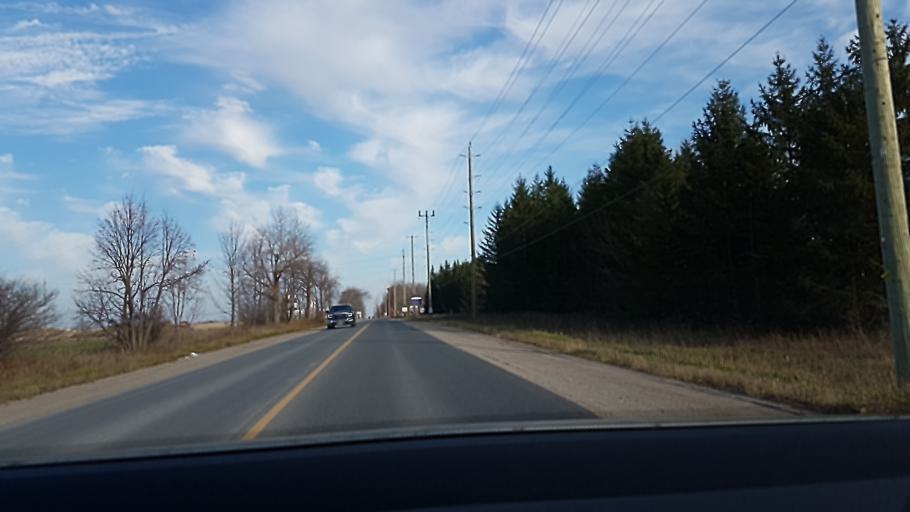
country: CA
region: Ontario
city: Barrie
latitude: 44.3774
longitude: -79.5565
